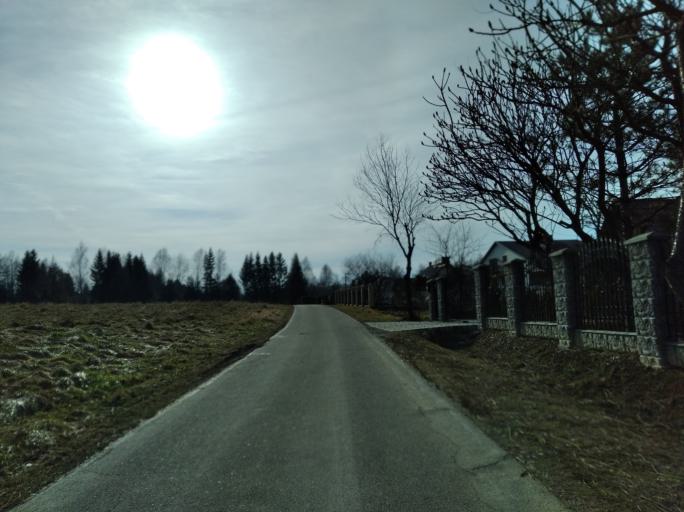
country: PL
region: Subcarpathian Voivodeship
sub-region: Powiat brzozowski
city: Grabownica Starzenska
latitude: 49.6461
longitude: 22.0674
